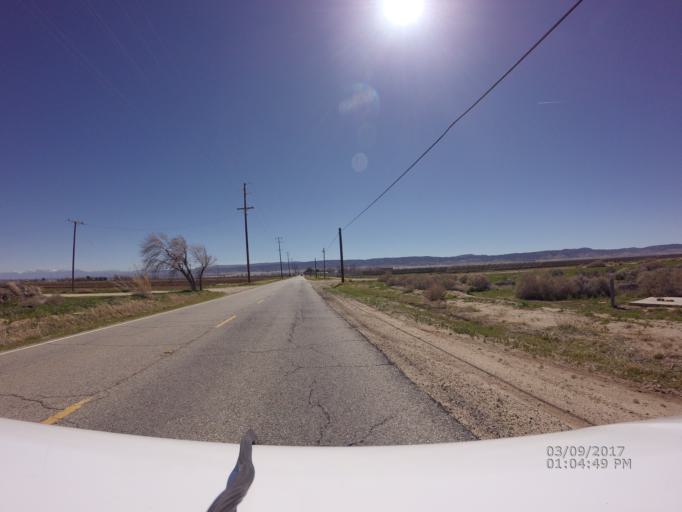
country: US
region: California
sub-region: Los Angeles County
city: Leona Valley
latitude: 34.7259
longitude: -118.2899
